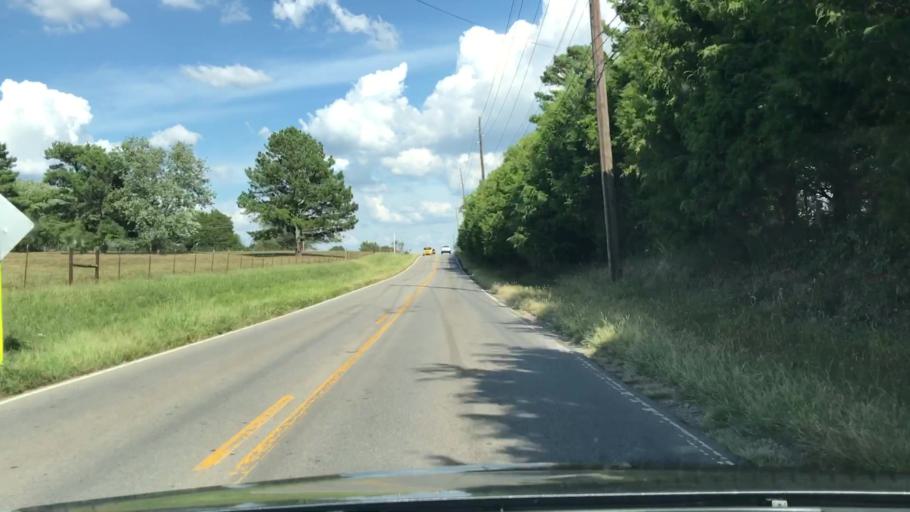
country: US
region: Alabama
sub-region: Madison County
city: Harvest
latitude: 34.8085
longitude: -86.7381
